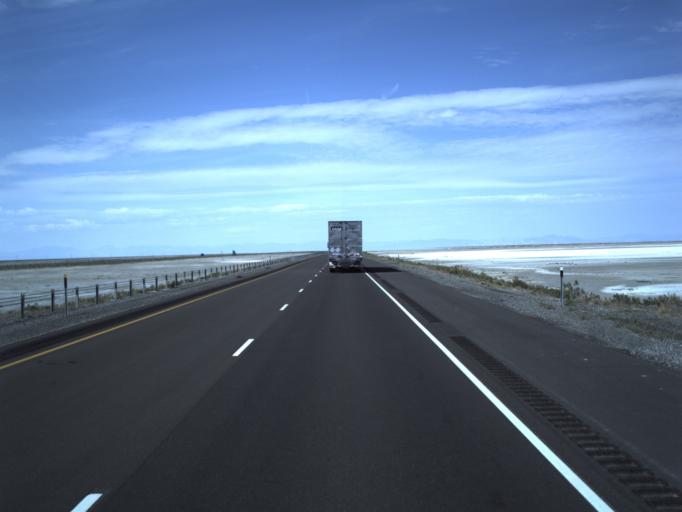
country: US
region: Utah
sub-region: Tooele County
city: Wendover
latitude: 40.7286
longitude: -113.3404
